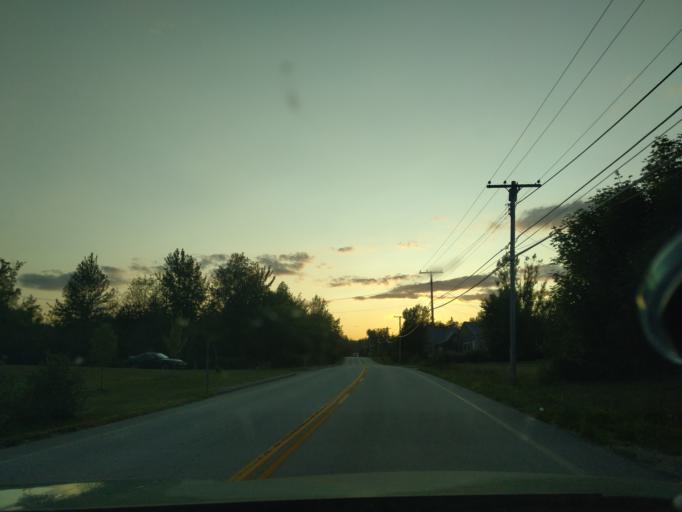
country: US
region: Maine
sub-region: Hancock County
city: Gouldsboro
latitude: 44.3903
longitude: -68.0428
